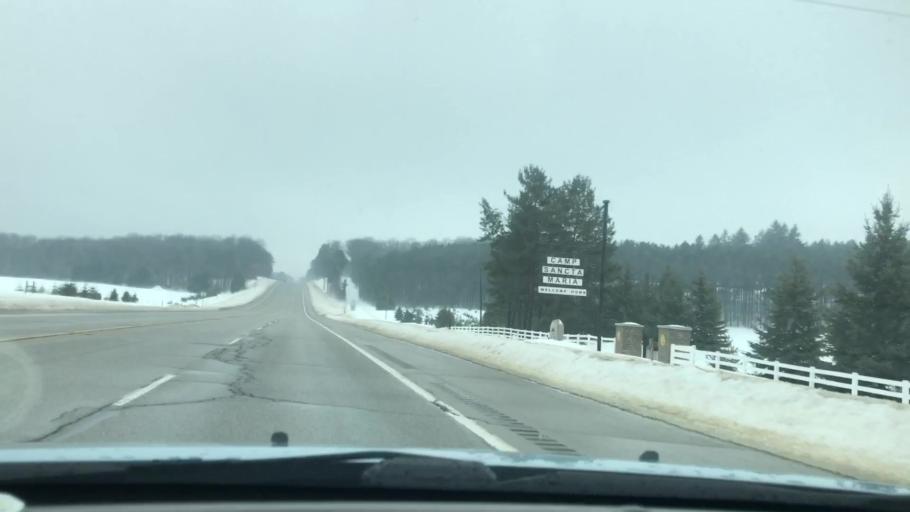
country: US
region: Michigan
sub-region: Otsego County
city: Gaylord
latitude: 45.0538
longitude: -84.7759
